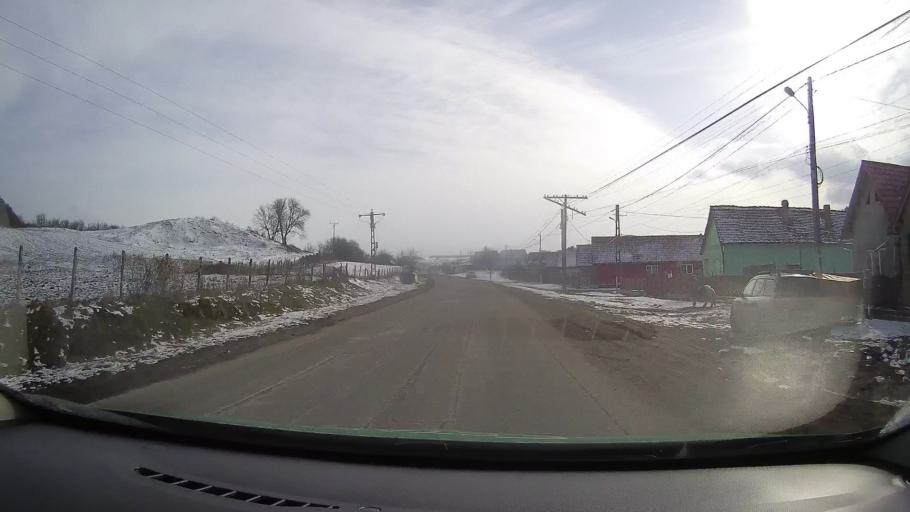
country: RO
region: Mures
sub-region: Comuna Apold
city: Apold
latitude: 46.1330
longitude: 24.8195
